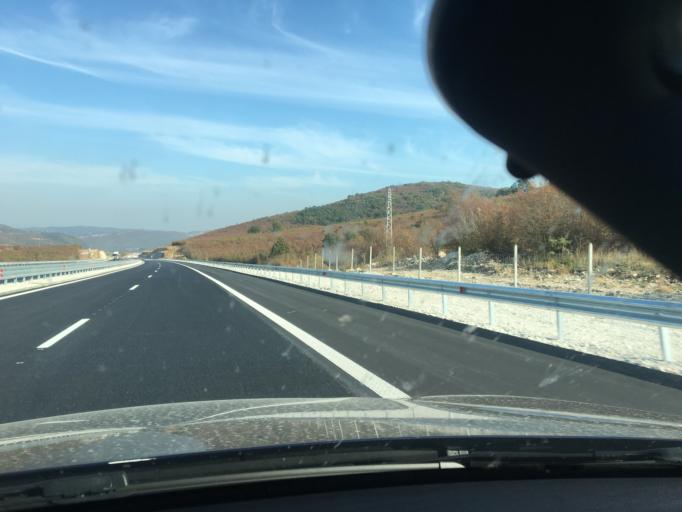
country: BG
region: Lovech
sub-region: Obshtina Yablanitsa
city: Yablanitsa
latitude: 43.0525
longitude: 24.1855
